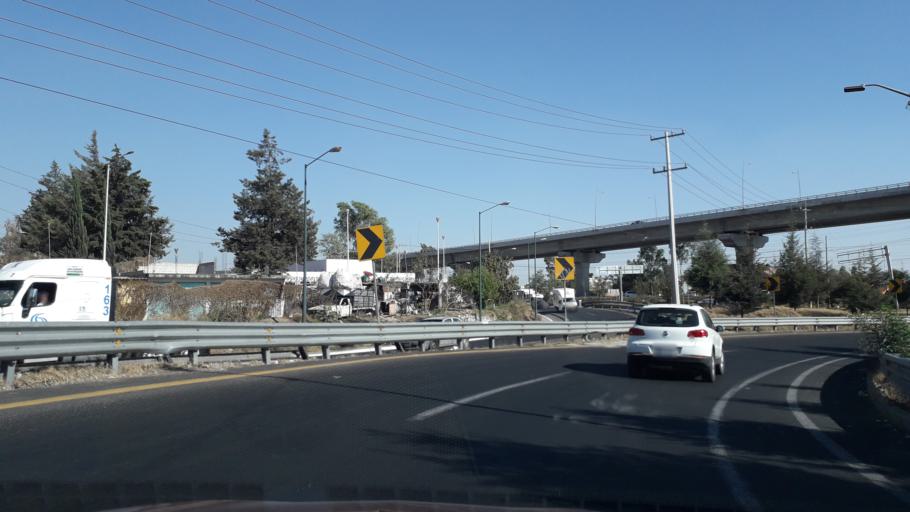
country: MX
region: Puebla
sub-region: Puebla
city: San Sebastian de Aparicio
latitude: 19.0850
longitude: -98.1867
